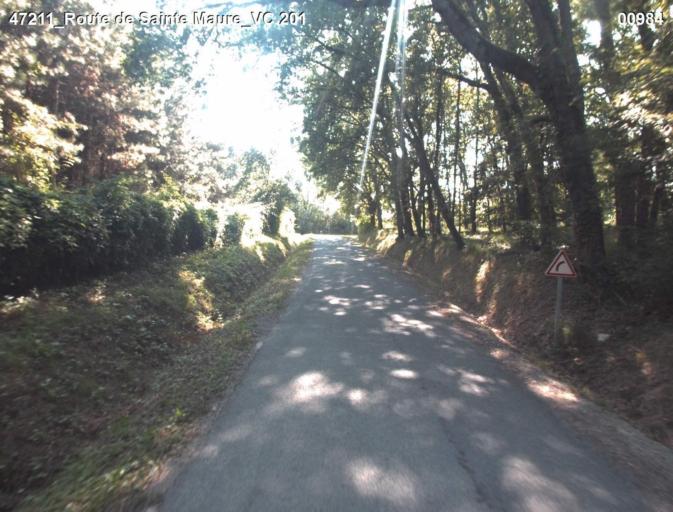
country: FR
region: Aquitaine
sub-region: Departement du Lot-et-Garonne
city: Mezin
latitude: 44.0314
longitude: 0.1929
